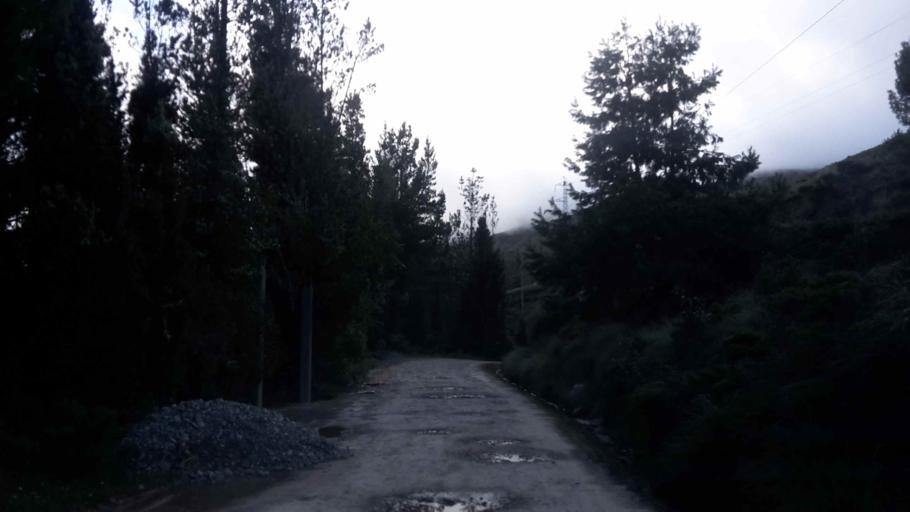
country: BO
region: Cochabamba
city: Colomi
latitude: -17.2381
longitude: -65.9013
